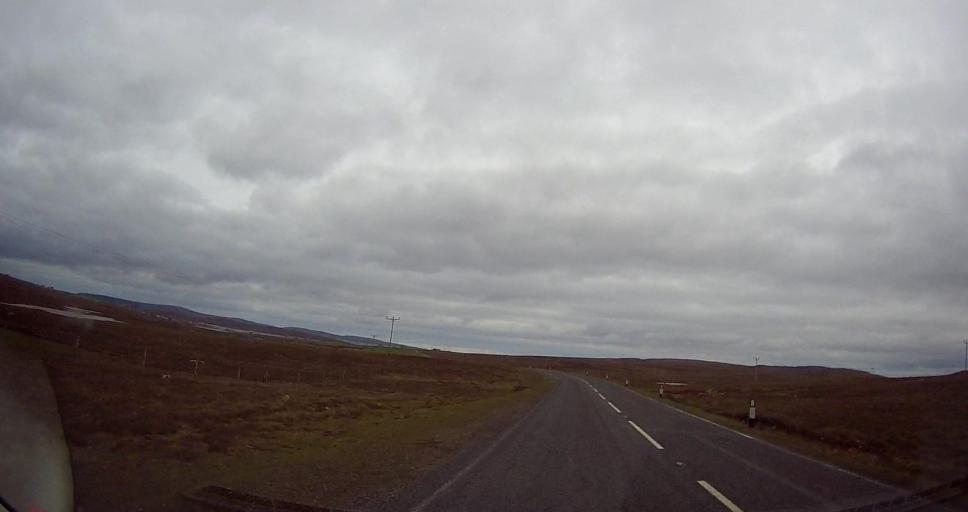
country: GB
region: Scotland
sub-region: Shetland Islands
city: Shetland
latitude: 60.7106
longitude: -0.9178
